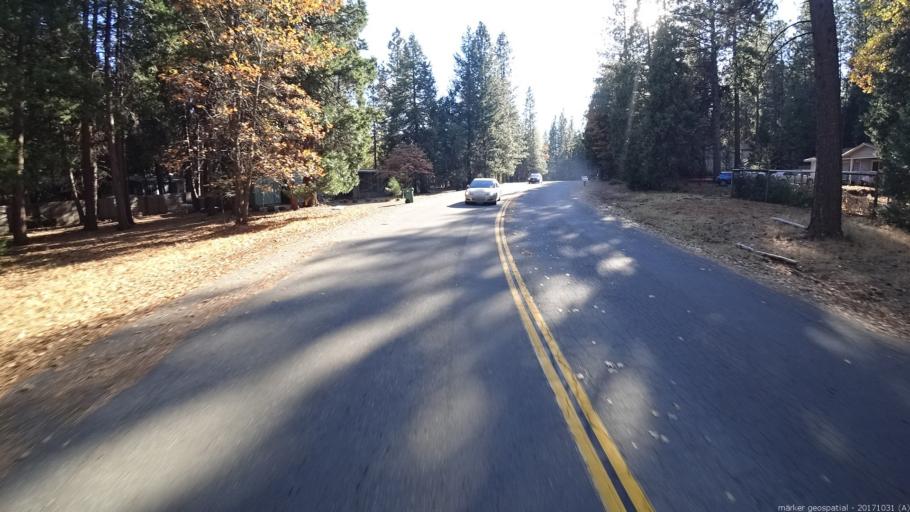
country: US
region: California
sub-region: Shasta County
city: Shingletown
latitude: 40.4993
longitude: -121.9103
